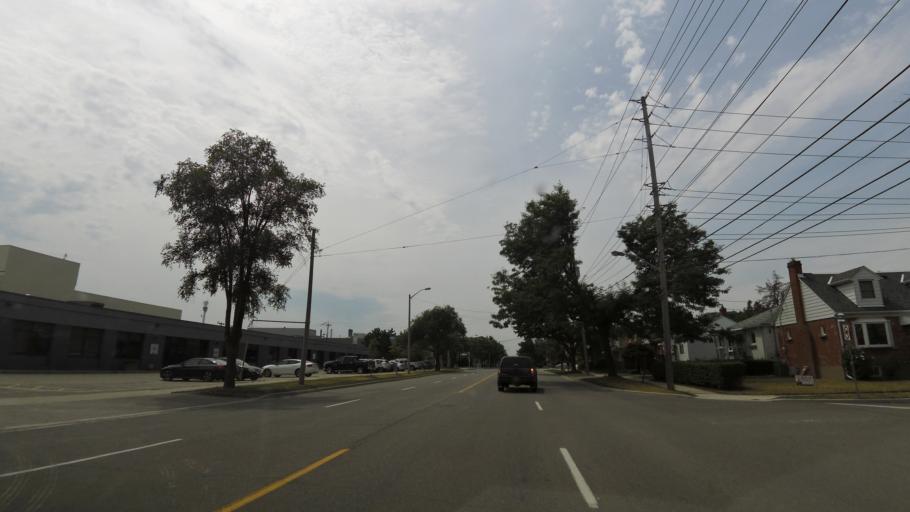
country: CA
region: Ontario
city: Etobicoke
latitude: 43.6052
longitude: -79.5300
